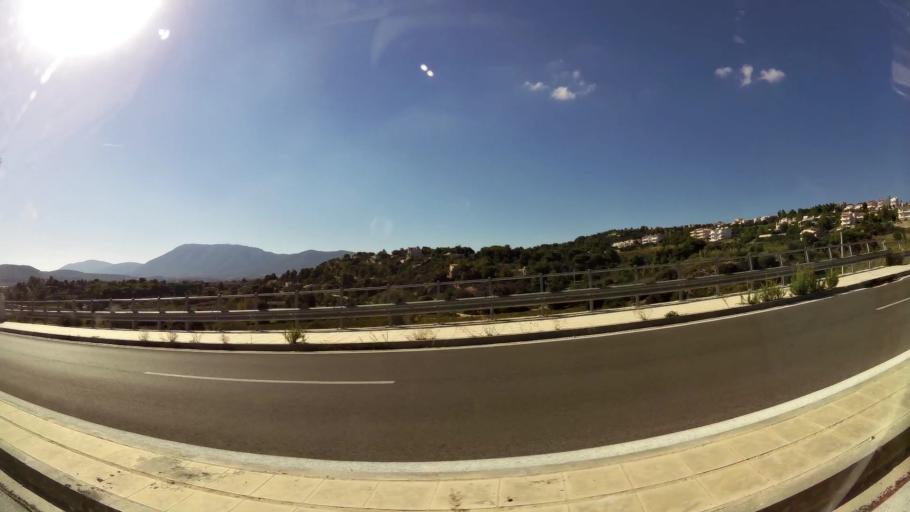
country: GR
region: Attica
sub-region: Nomarchia Anatolikis Attikis
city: Dhrafi
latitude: 38.0119
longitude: 23.9113
